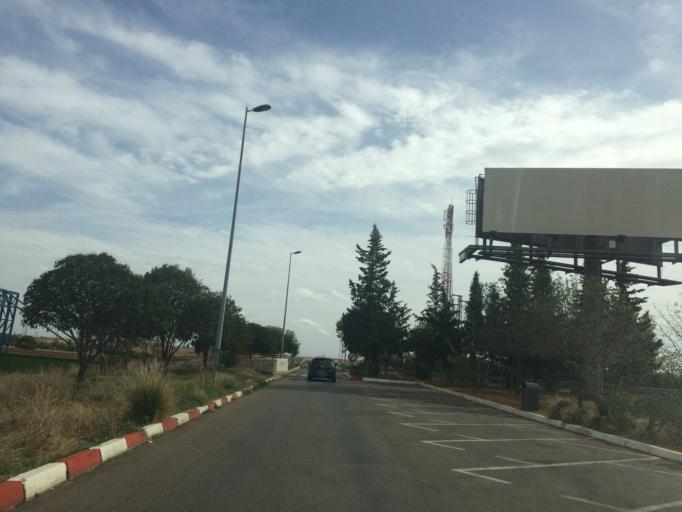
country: MA
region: Meknes-Tafilalet
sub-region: Meknes
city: Meknes
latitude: 33.8320
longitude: -5.5697
